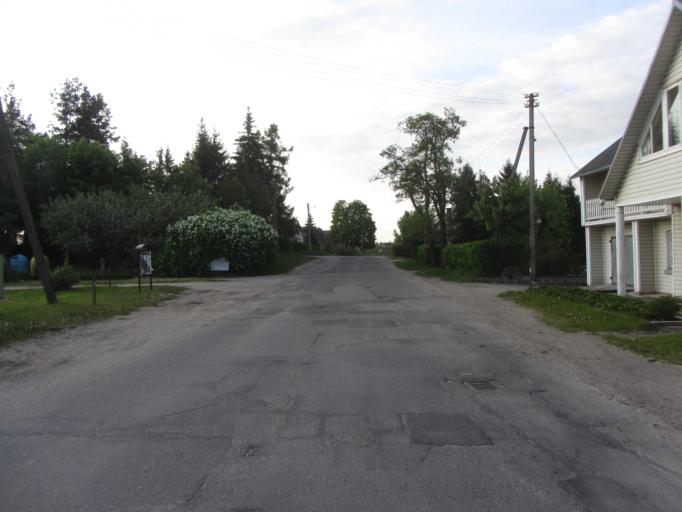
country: LT
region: Utenos apskritis
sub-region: Utena
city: Utena
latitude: 55.4964
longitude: 25.5877
